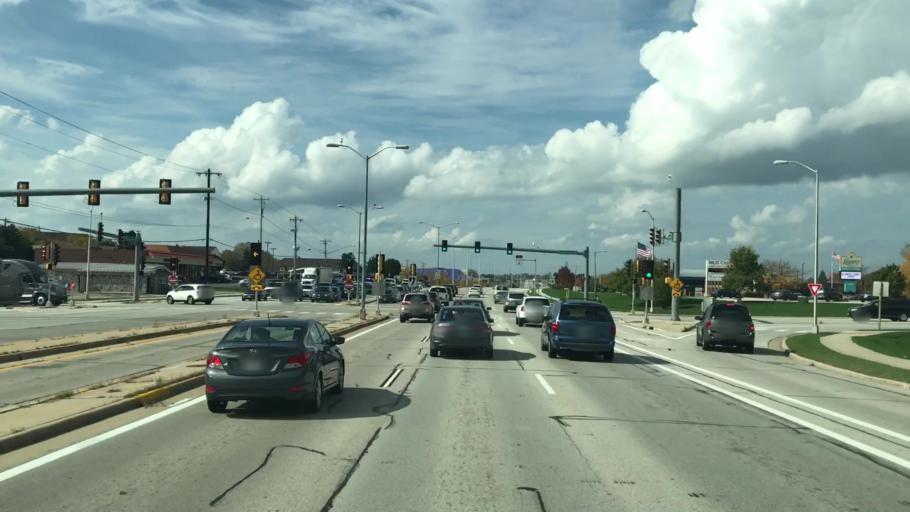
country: US
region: Wisconsin
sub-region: Waukesha County
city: Brookfield
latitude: 43.0363
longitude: -88.1460
